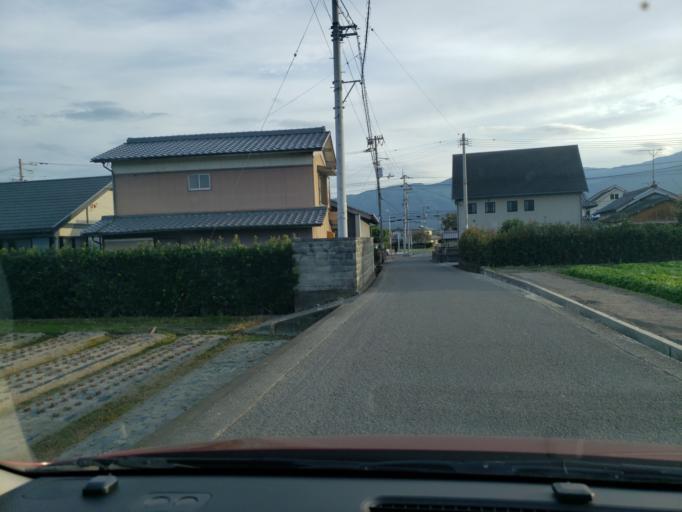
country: JP
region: Tokushima
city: Wakimachi
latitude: 34.0753
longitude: 134.2277
